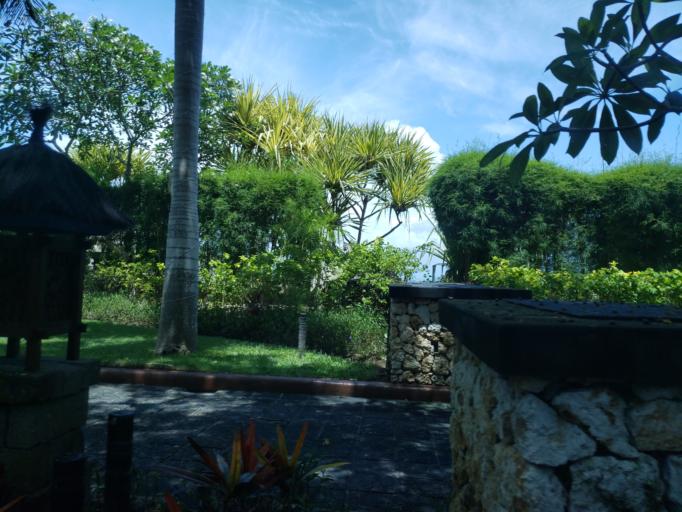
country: ID
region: Bali
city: Jimbaran
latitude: -8.7843
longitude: 115.1592
